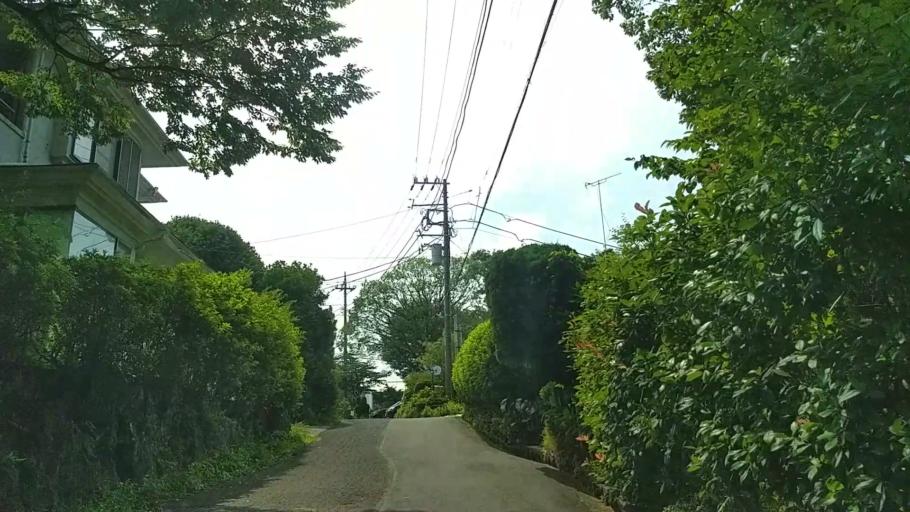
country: JP
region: Shizuoka
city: Ito
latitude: 34.9175
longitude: 139.1053
